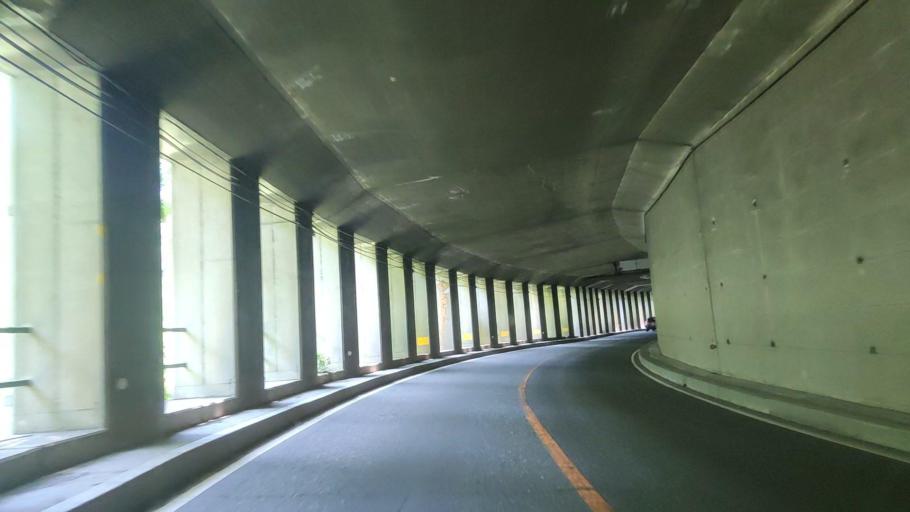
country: JP
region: Niigata
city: Itoigawa
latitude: 36.9162
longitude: 137.8735
